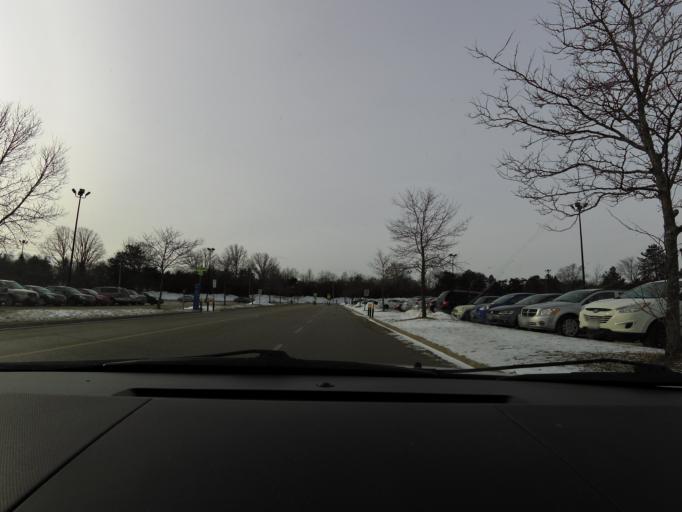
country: CA
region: Ontario
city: Waterloo
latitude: 43.4679
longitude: -80.5381
